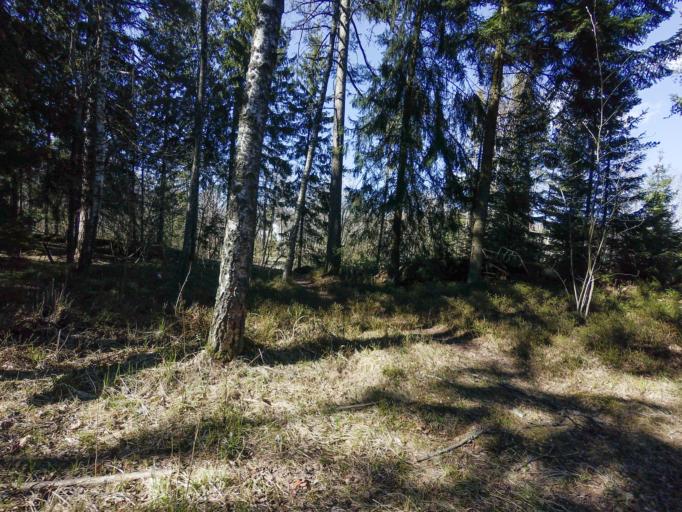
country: FI
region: Uusimaa
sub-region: Helsinki
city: Vantaa
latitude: 60.1719
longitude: 25.0591
